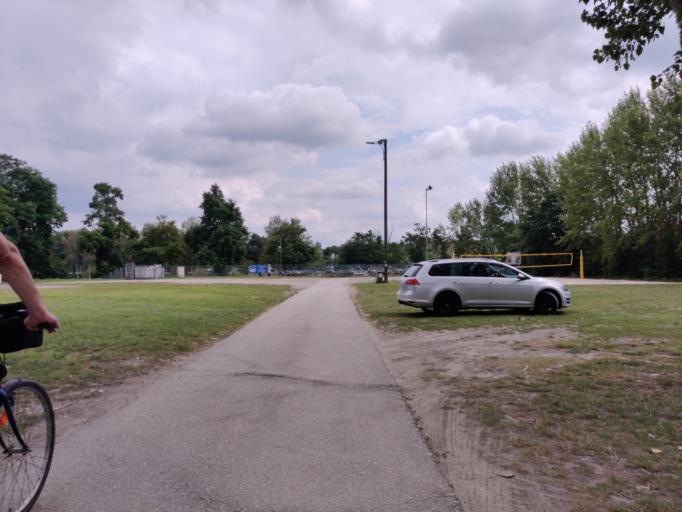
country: AT
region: Lower Austria
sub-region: Politischer Bezirk Melk
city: Melk
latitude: 48.2309
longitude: 15.3096
